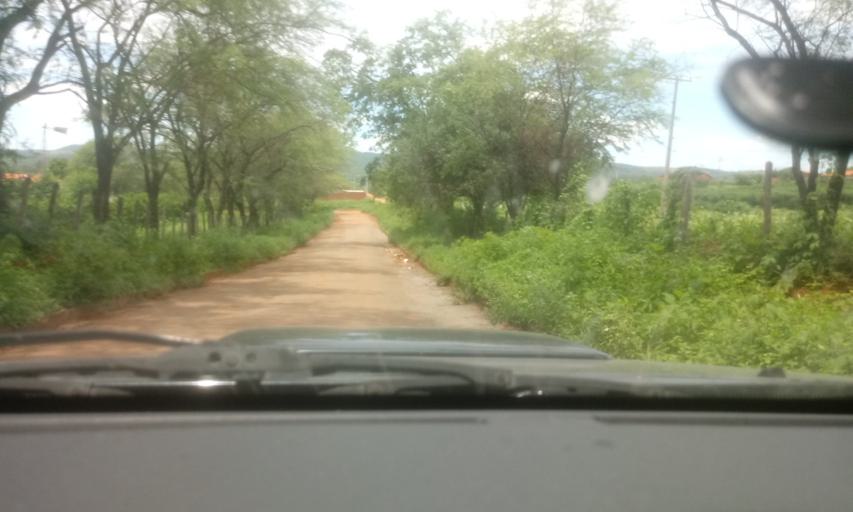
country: BR
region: Bahia
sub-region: Riacho De Santana
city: Riacho de Santana
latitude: -13.6031
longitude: -42.9466
